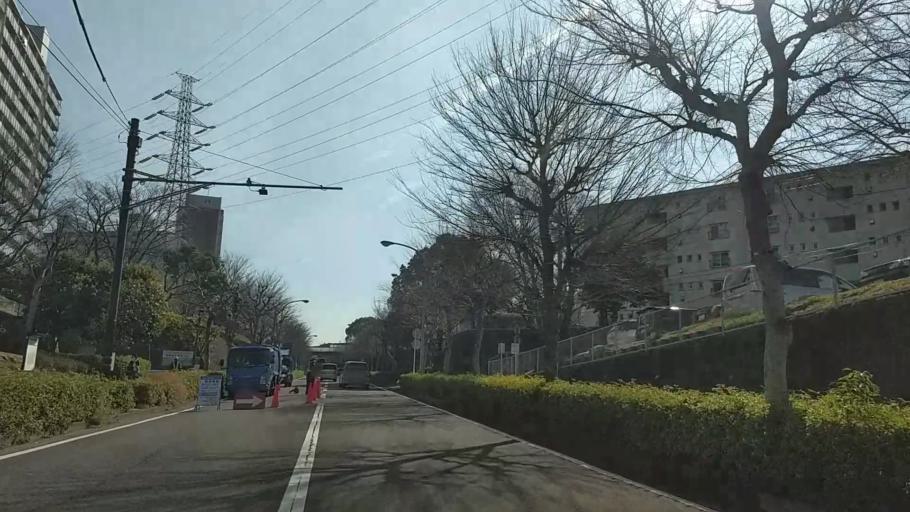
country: JP
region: Kanagawa
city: Kamakura
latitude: 35.3736
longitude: 139.5824
